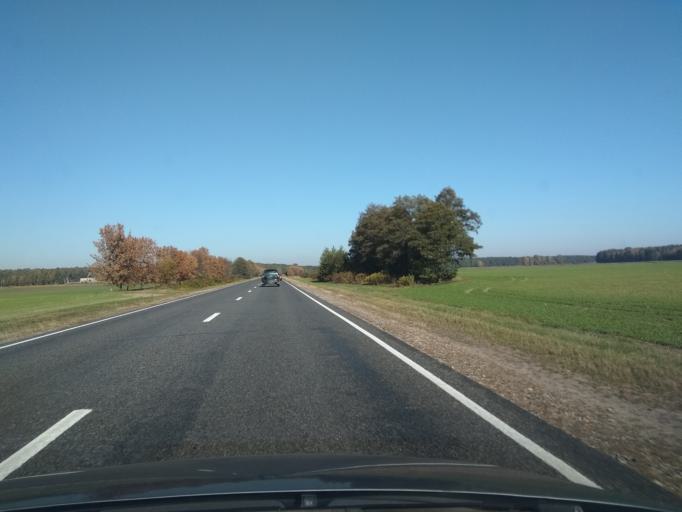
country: BY
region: Brest
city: Kobryn
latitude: 52.1222
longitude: 24.3053
